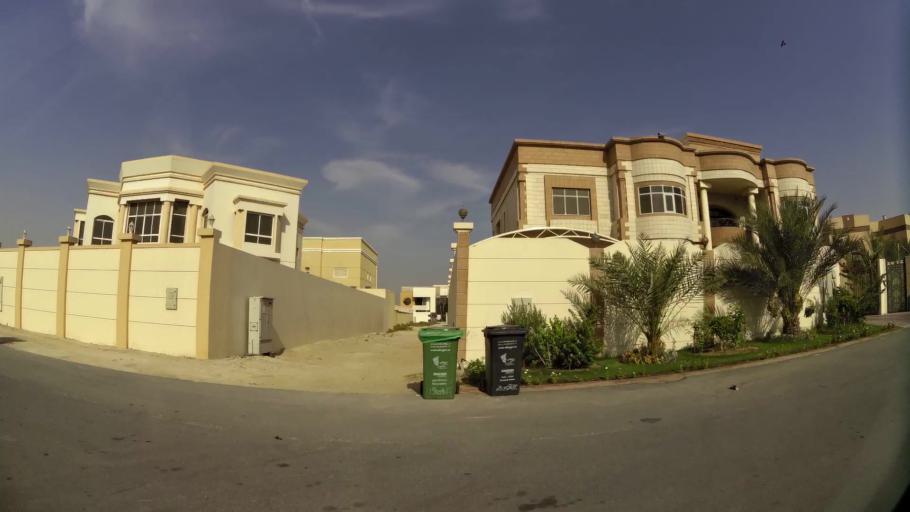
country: AE
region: Ash Shariqah
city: Sharjah
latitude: 25.2425
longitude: 55.4153
